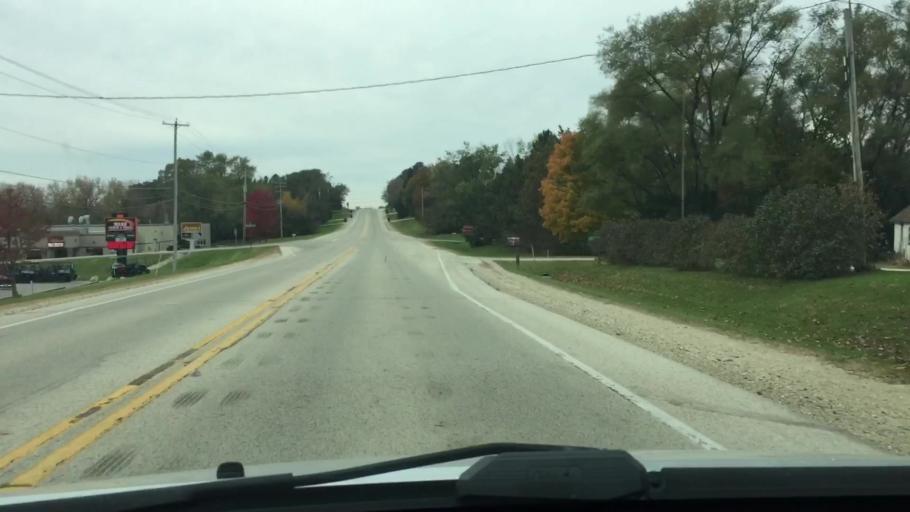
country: US
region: Wisconsin
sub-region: Waukesha County
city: Big Bend
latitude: 42.9201
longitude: -88.2047
